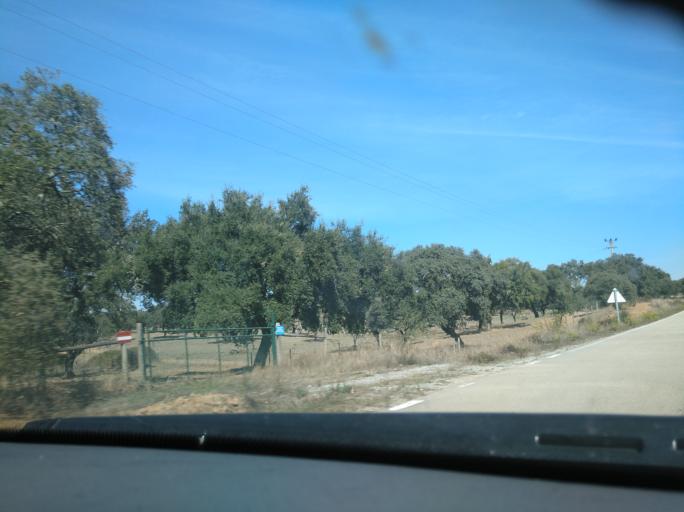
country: PT
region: Evora
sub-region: Arraiolos
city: Arraiolos
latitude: 38.6867
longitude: -8.0896
